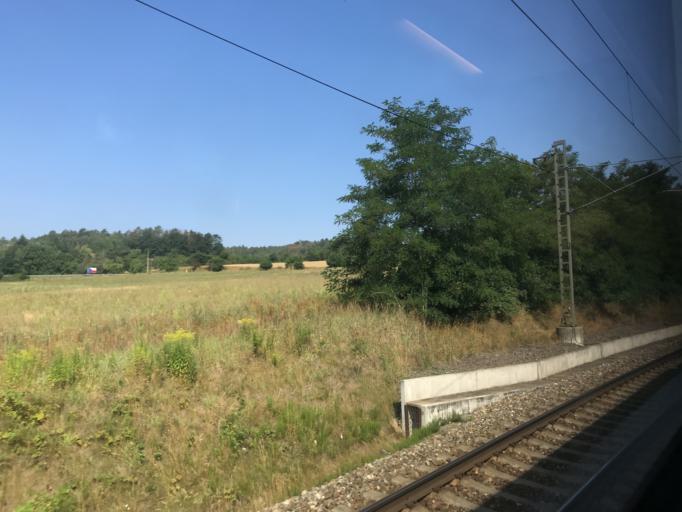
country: CZ
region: Central Bohemia
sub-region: Okres Benesov
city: Cercany
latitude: 49.8568
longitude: 14.6959
